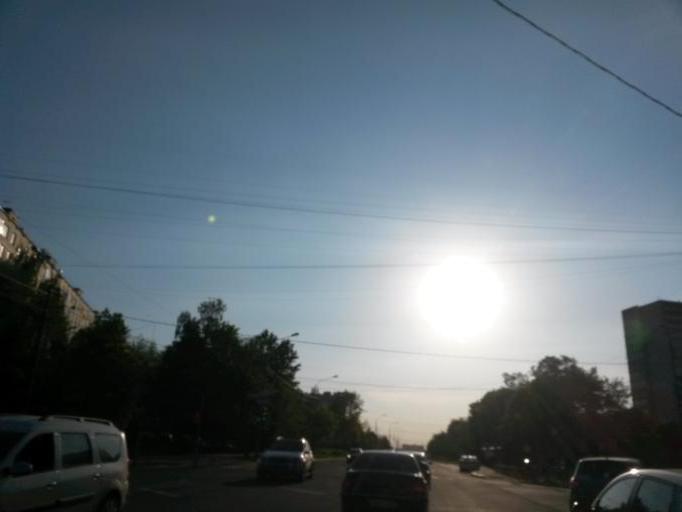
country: RU
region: Moskovskaya
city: Biryulevo Zapadnoye
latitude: 55.5872
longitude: 37.6462
